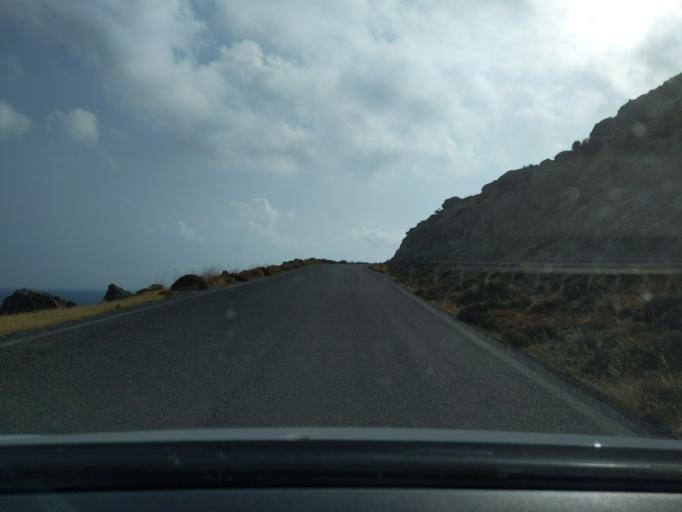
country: GR
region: Crete
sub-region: Nomos Lasithiou
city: Palekastro
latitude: 35.0897
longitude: 26.2633
